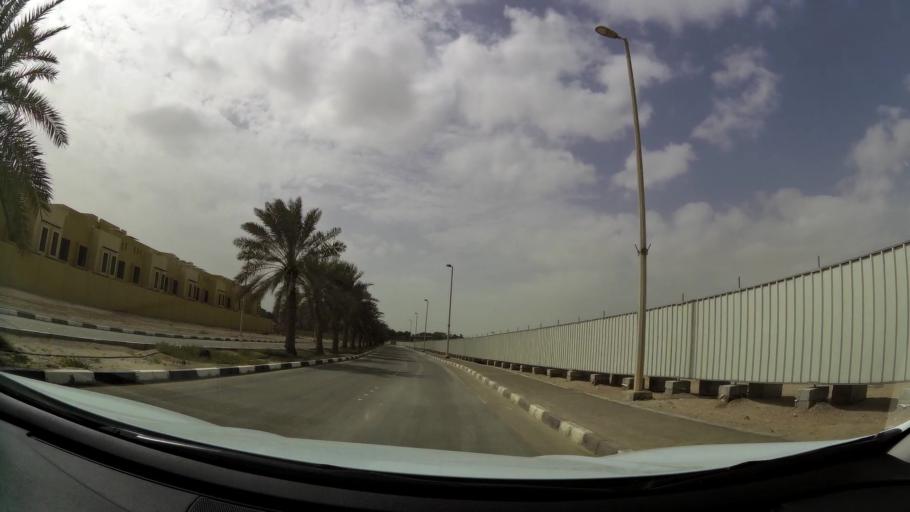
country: AE
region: Abu Dhabi
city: Abu Dhabi
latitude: 24.4004
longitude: 54.4870
